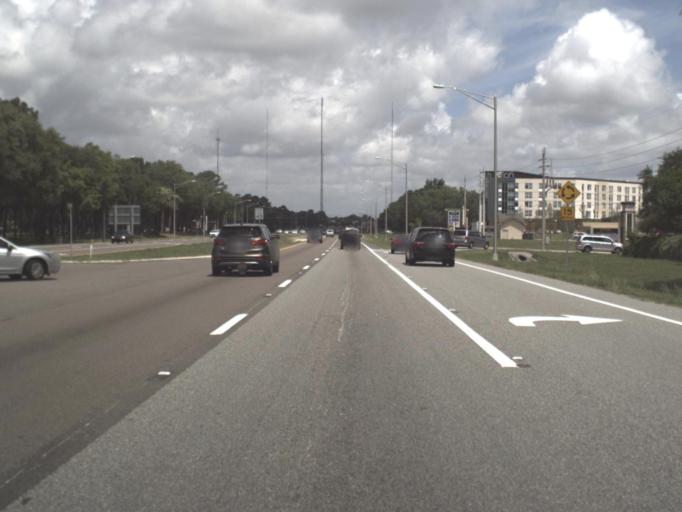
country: US
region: Florida
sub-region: Duval County
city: Jacksonville
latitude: 30.2566
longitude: -81.5544
